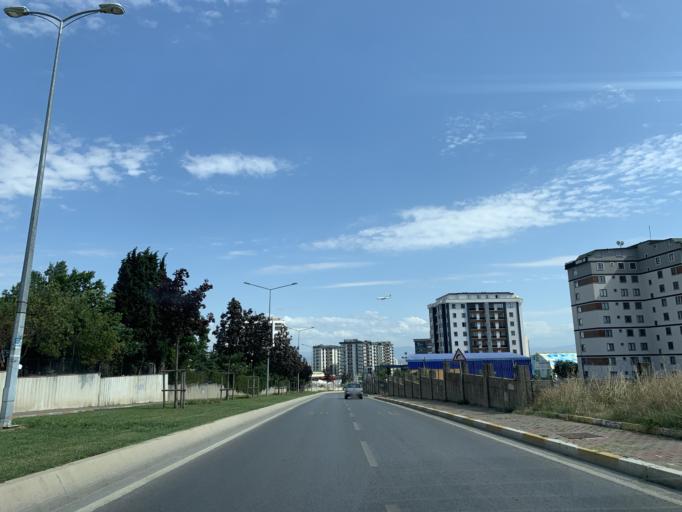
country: TR
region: Istanbul
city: Pendik
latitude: 40.8942
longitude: 29.2617
